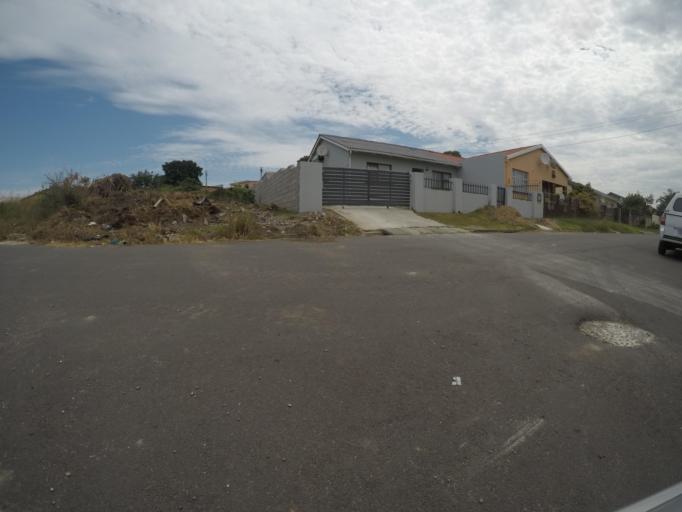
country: ZA
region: Eastern Cape
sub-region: Buffalo City Metropolitan Municipality
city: East London
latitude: -32.9929
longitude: 27.8805
